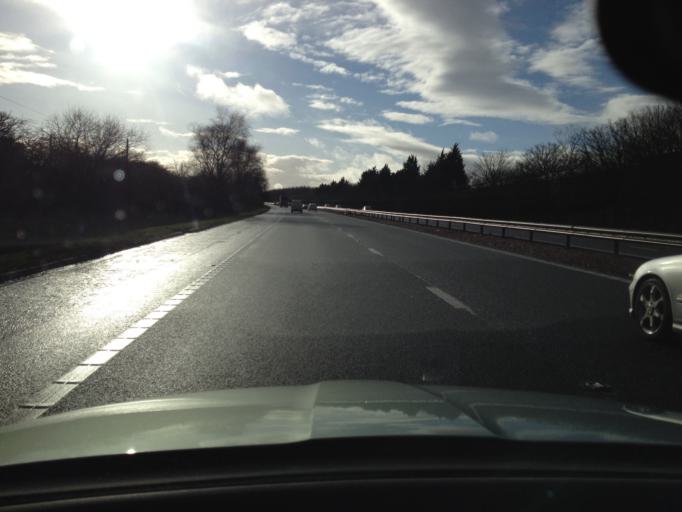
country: GB
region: Scotland
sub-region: West Lothian
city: Broxburn
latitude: 55.9201
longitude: -3.4910
